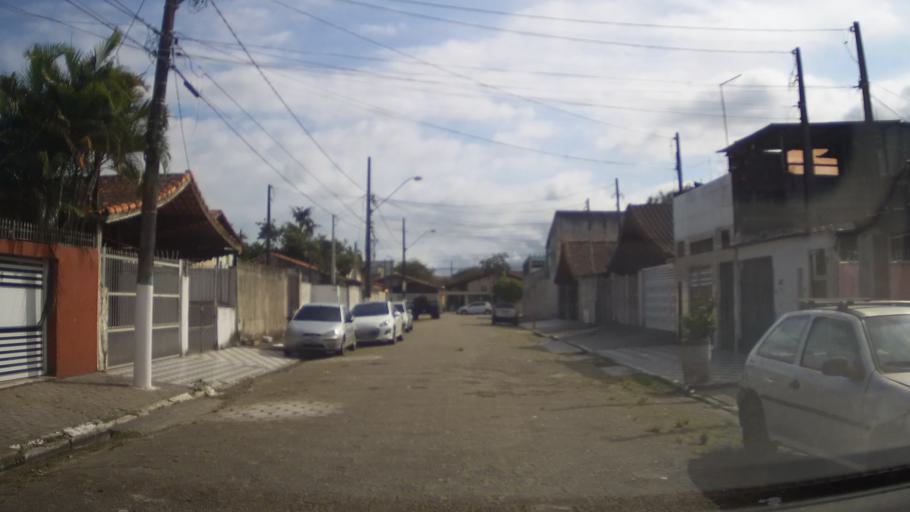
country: BR
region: Sao Paulo
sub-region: Praia Grande
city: Praia Grande
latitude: -24.0177
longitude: -46.4641
